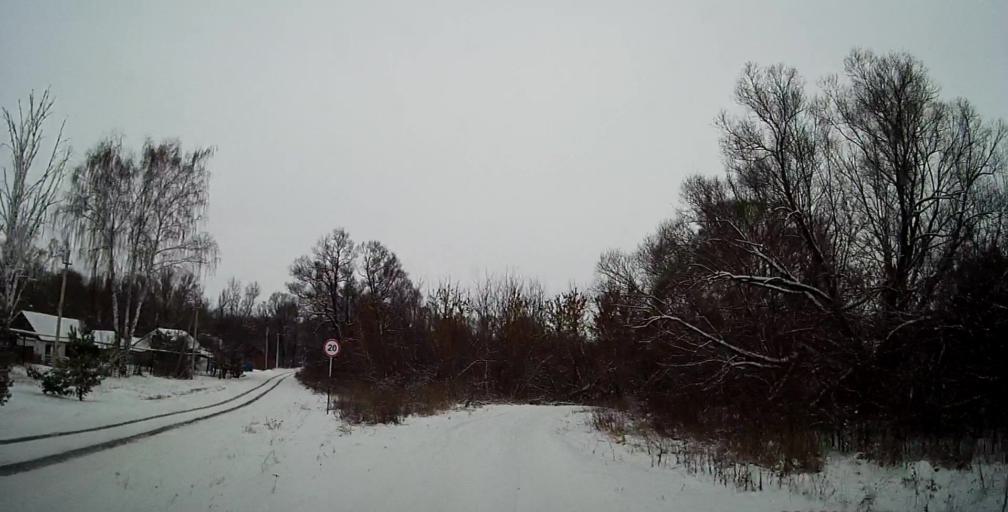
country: RU
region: Lipetsk
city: Lev Tolstoy
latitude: 53.3377
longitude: 39.5845
